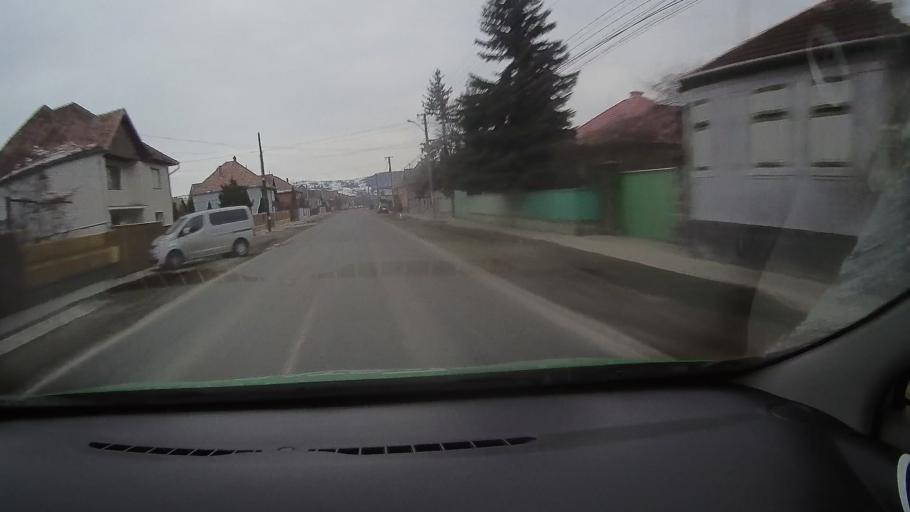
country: RO
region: Harghita
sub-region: Comuna Feliceni
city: Feliceni
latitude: 46.2718
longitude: 25.2763
